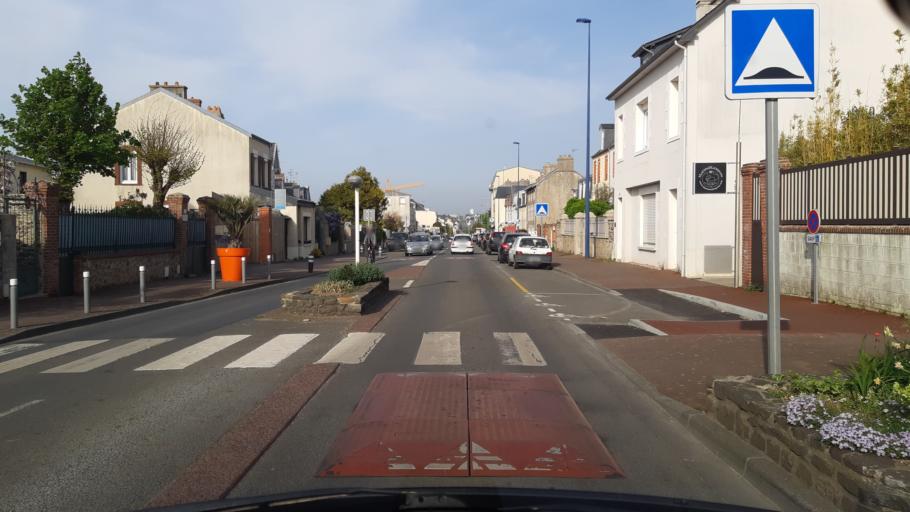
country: FR
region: Lower Normandy
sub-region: Departement de la Manche
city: Granville
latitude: 48.8418
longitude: -1.5909
